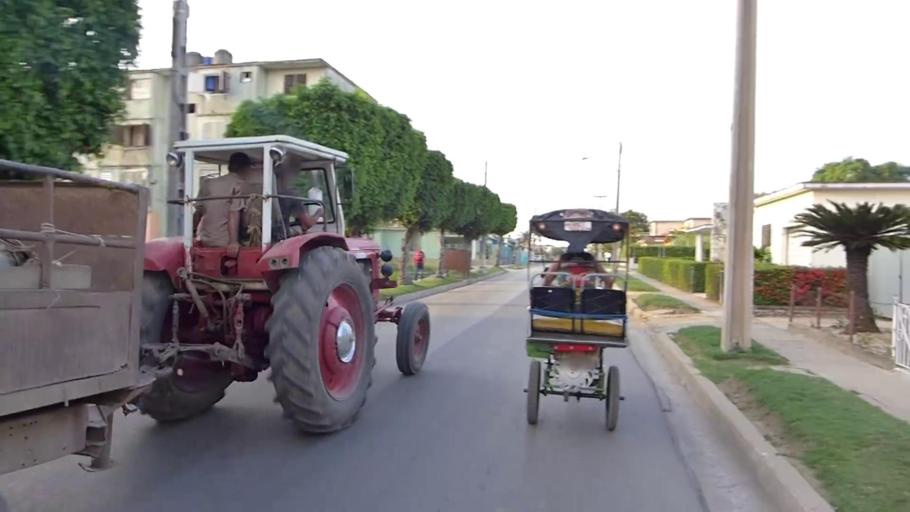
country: CU
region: Camaguey
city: Camaguey
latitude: 21.3805
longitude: -77.9369
